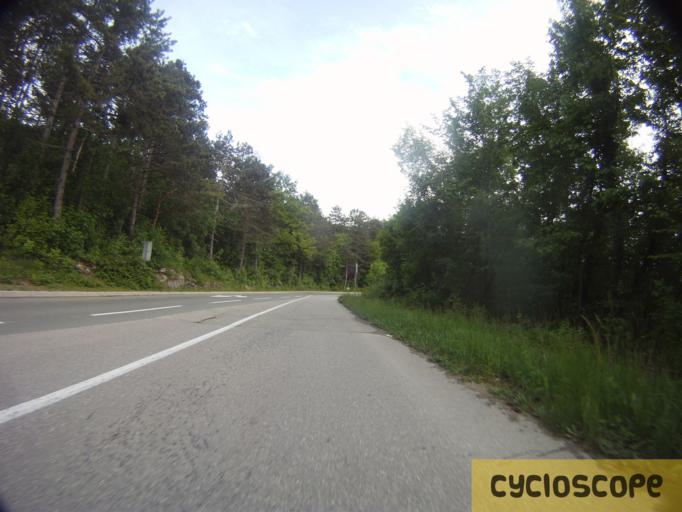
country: HR
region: Primorsko-Goranska
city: Klana
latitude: 45.4339
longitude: 14.3673
